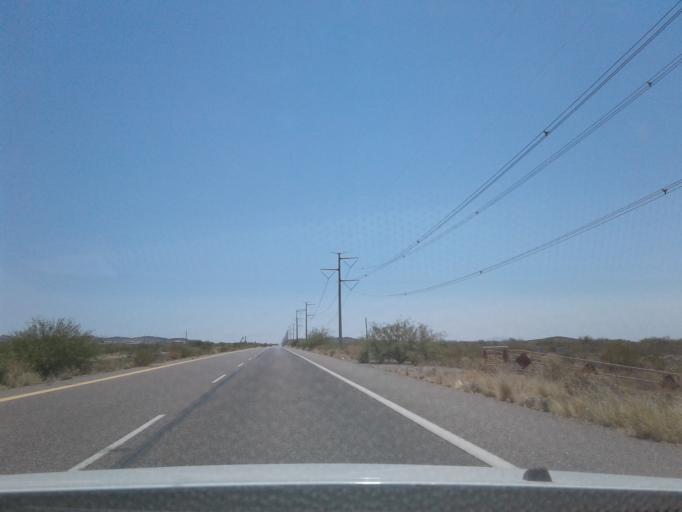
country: US
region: Arizona
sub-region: Maricopa County
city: Laveen
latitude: 33.2909
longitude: -112.1120
